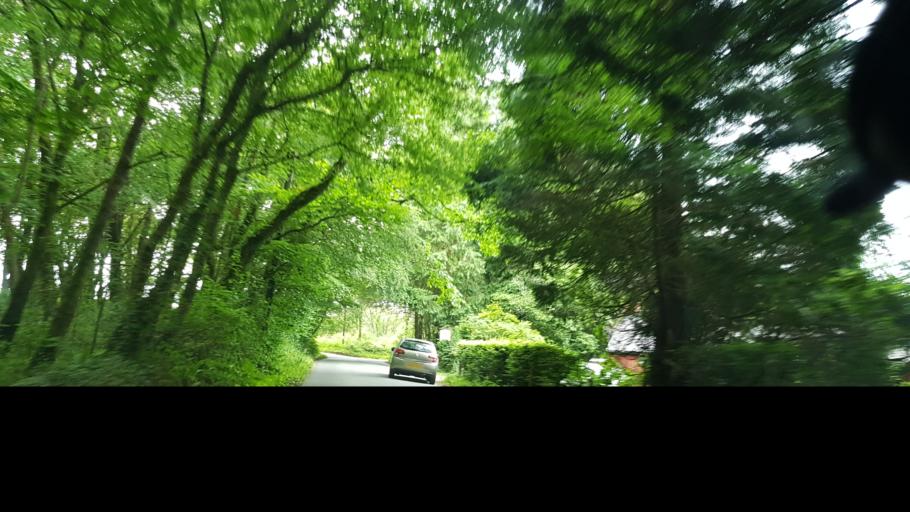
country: GB
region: Wales
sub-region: Pembrokeshire
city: Hook
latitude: 51.7944
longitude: -4.9048
